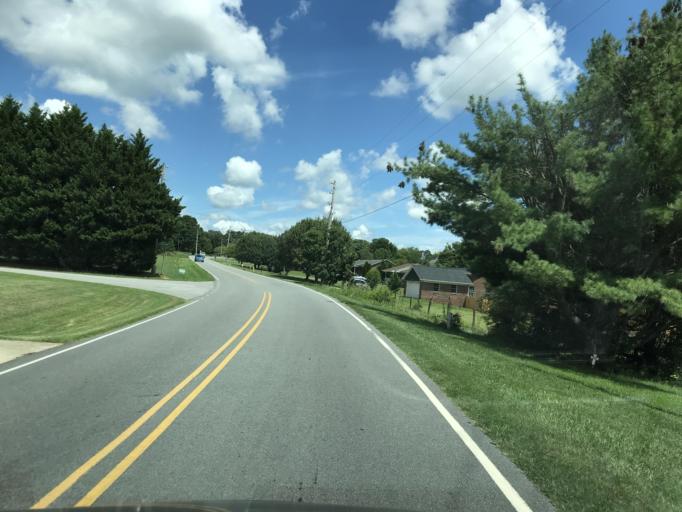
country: US
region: North Carolina
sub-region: Lincoln County
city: Lincolnton
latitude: 35.5042
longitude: -81.2152
